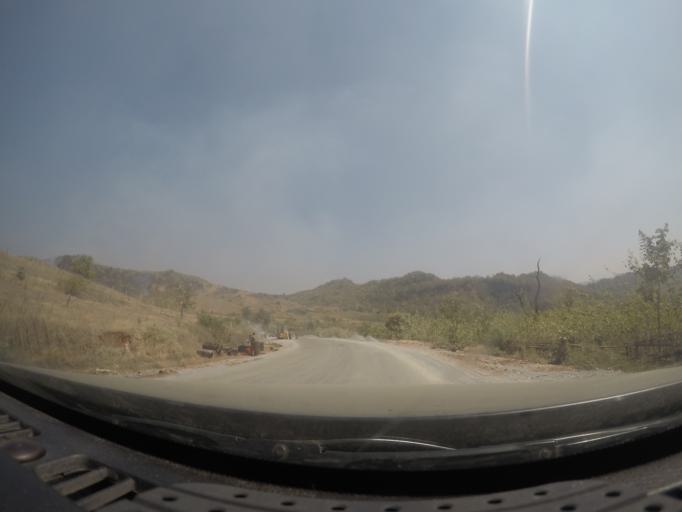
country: MM
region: Shan
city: Taunggyi
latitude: 20.8168
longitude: 97.2175
